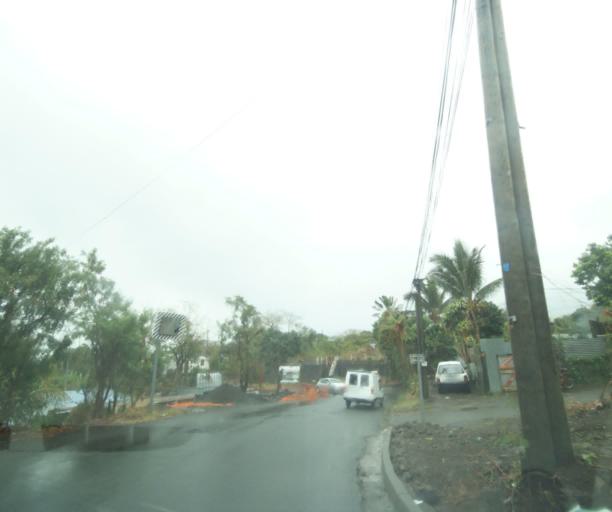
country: RE
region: Reunion
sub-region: Reunion
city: La Possession
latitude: -20.9760
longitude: 55.3323
